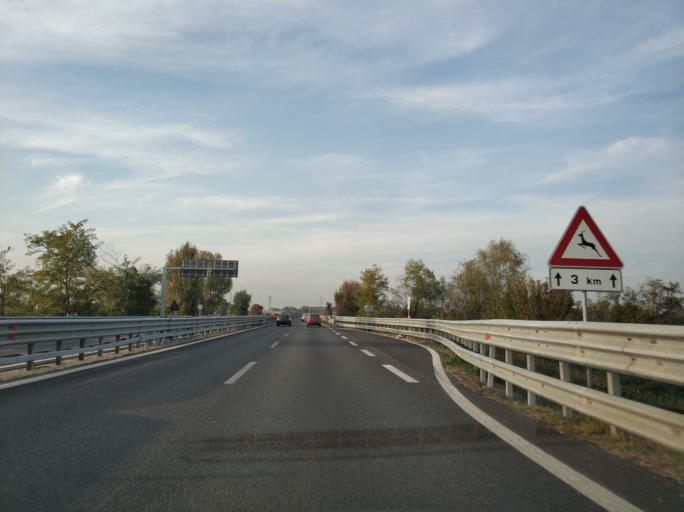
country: IT
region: Piedmont
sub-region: Provincia di Torino
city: Borgaro Torinese
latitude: 45.1420
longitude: 7.6908
